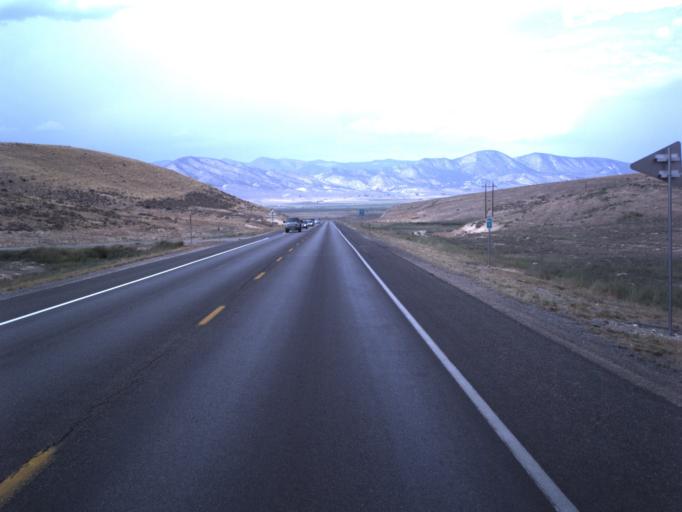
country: US
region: Utah
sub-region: Sanpete County
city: Gunnison
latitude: 39.1704
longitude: -111.8274
